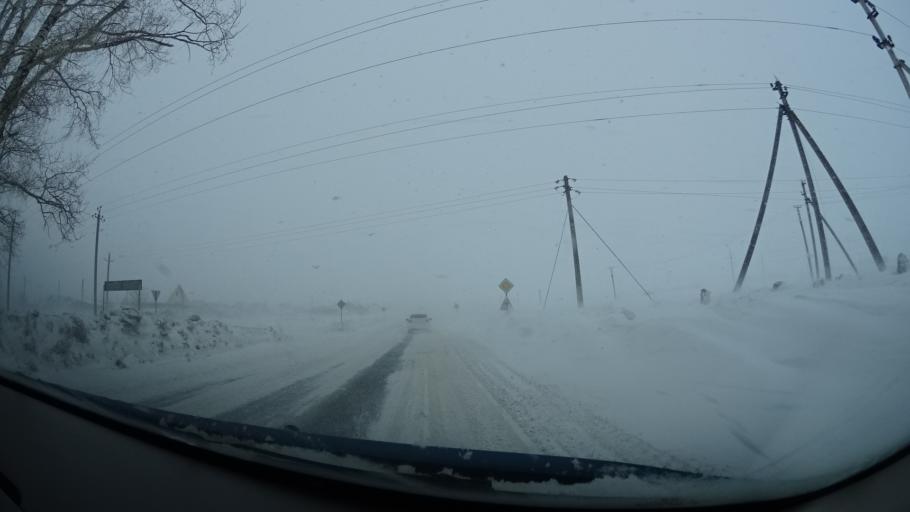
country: RU
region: Perm
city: Kuyeda
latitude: 56.4214
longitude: 55.5848
